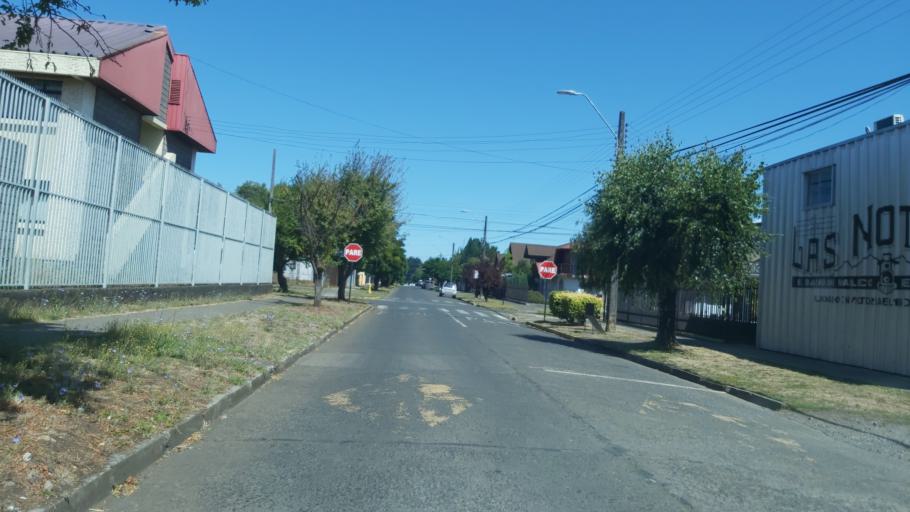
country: CL
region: Araucania
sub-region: Provincia de Malleco
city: Victoria
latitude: -38.2314
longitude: -72.3317
